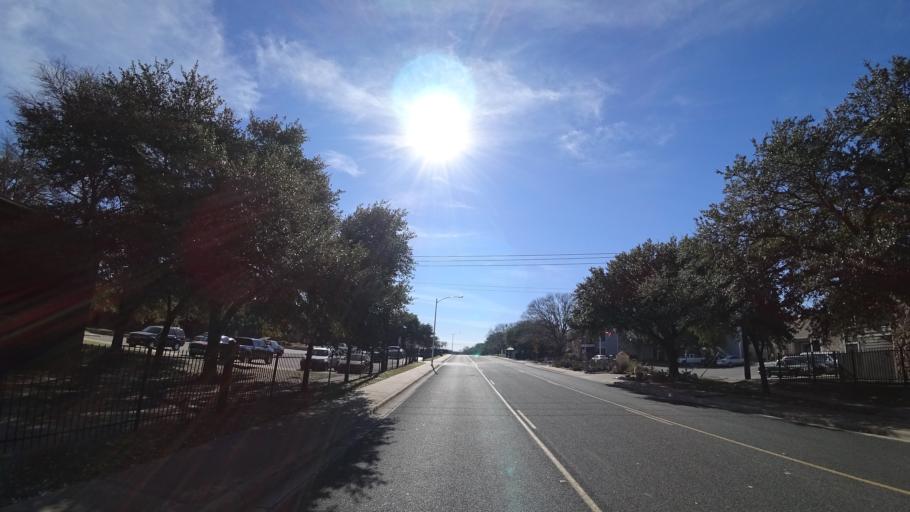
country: US
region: Texas
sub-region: Travis County
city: Wells Branch
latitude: 30.3750
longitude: -97.7115
